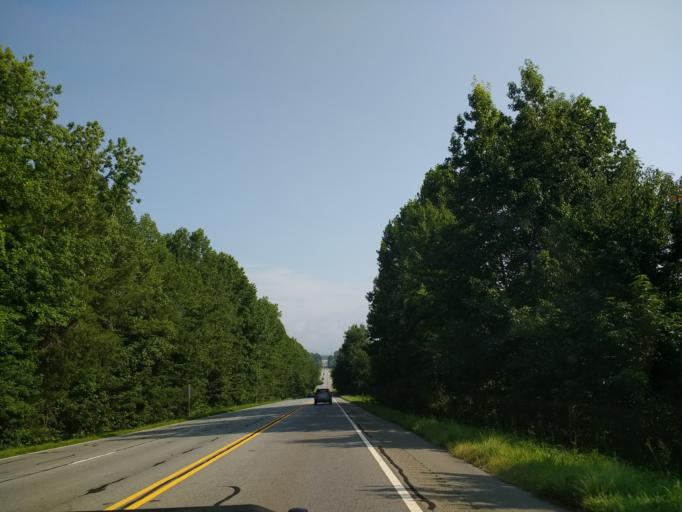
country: US
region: Georgia
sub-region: White County
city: Cleveland
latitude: 34.5288
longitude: -83.7556
